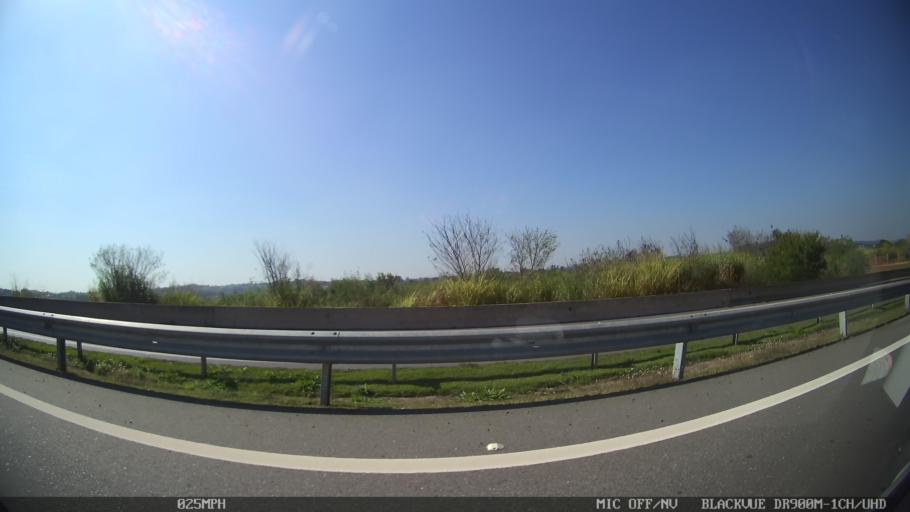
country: BR
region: Sao Paulo
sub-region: Valinhos
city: Valinhos
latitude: -23.0140
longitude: -47.0832
